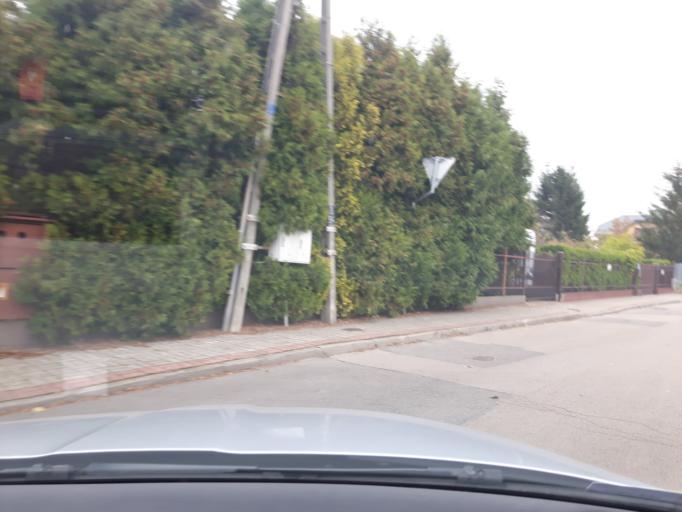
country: PL
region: Masovian Voivodeship
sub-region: Powiat wolominski
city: Zabki
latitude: 52.2894
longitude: 21.0941
